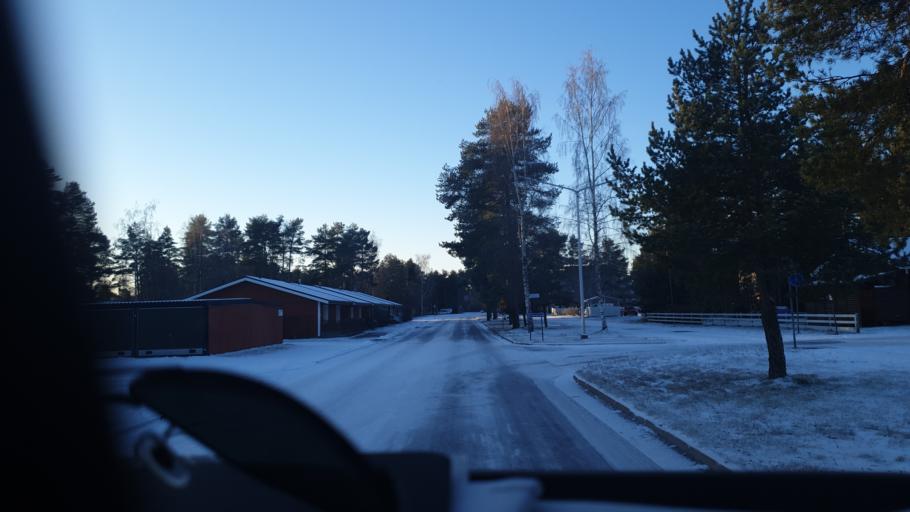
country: FI
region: Central Ostrobothnia
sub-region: Kokkola
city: Kokkola
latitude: 63.8237
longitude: 23.0787
